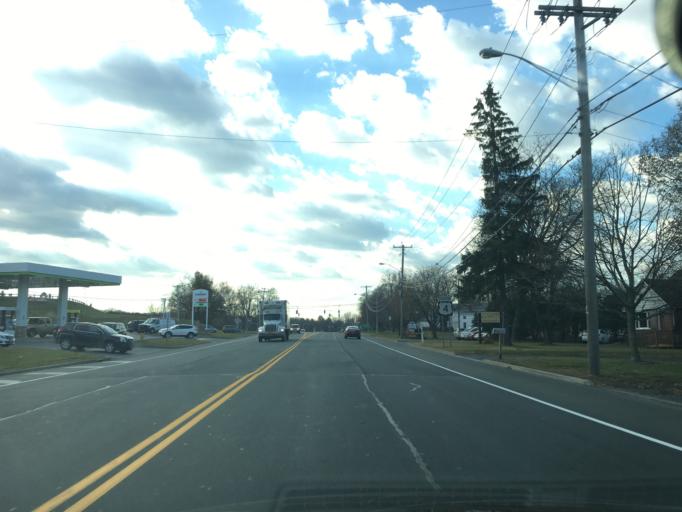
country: US
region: New York
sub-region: Albany County
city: Menands
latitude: 42.6584
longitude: -73.6930
